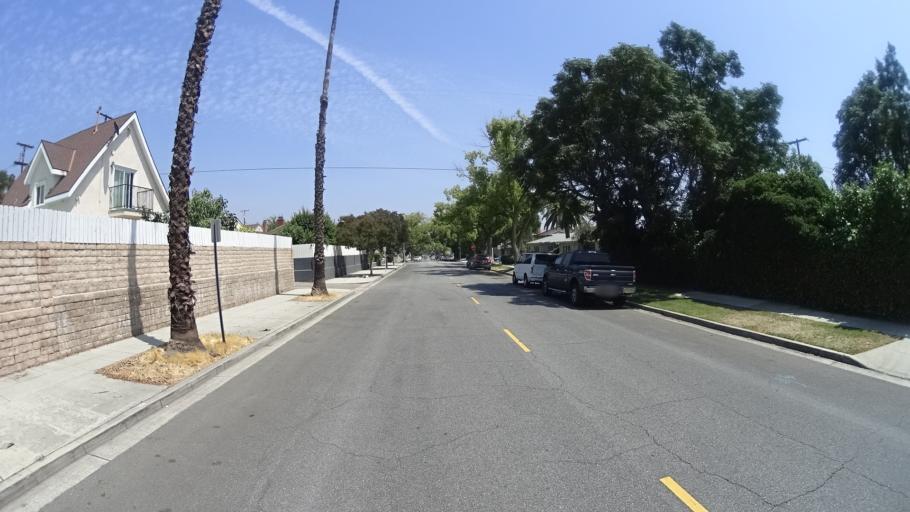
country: US
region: California
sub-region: Los Angeles County
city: Burbank
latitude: 34.1902
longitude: -118.3103
